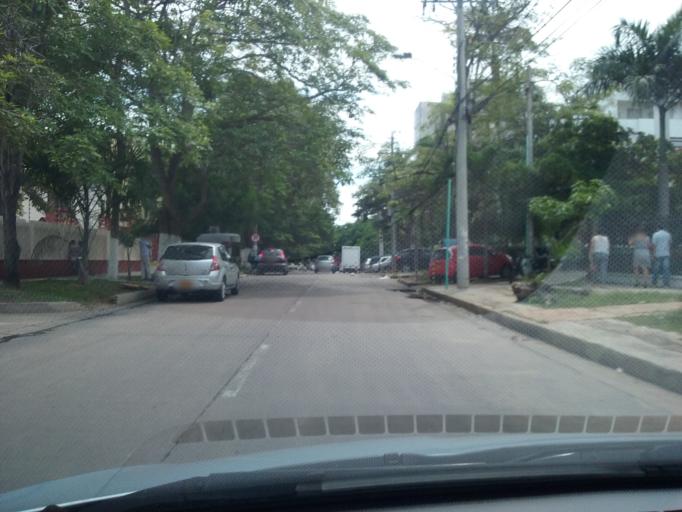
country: CO
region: Atlantico
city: Barranquilla
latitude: 11.0021
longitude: -74.8003
